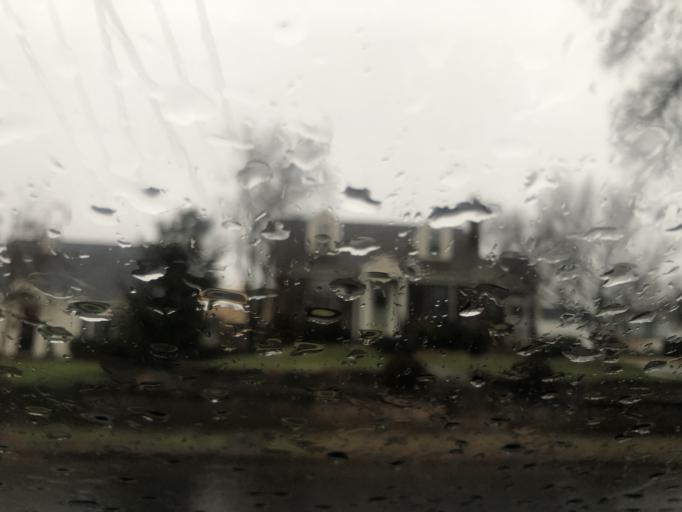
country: US
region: Tennessee
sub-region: Davidson County
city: Nashville
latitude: 36.1269
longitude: -86.8025
